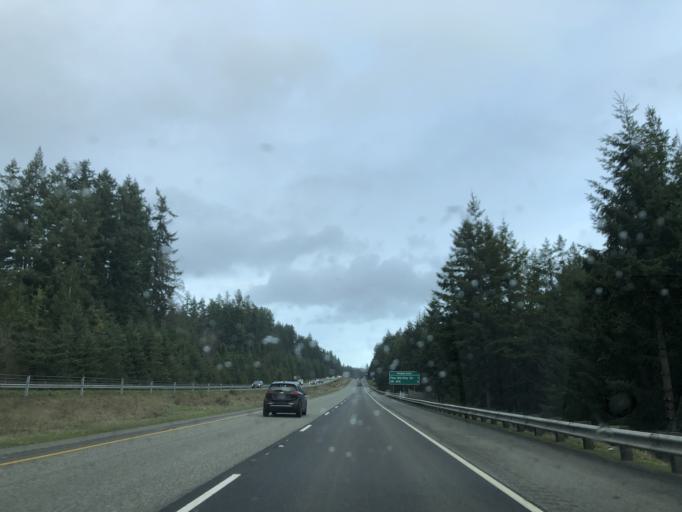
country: US
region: Washington
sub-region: Kitsap County
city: Poulsbo
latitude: 47.7342
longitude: -122.6746
